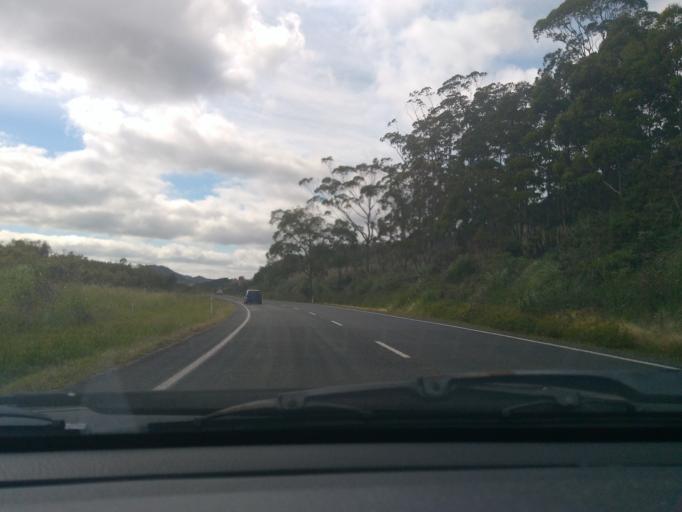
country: NZ
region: Northland
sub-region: Far North District
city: Taipa
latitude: -35.0085
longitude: 173.5402
